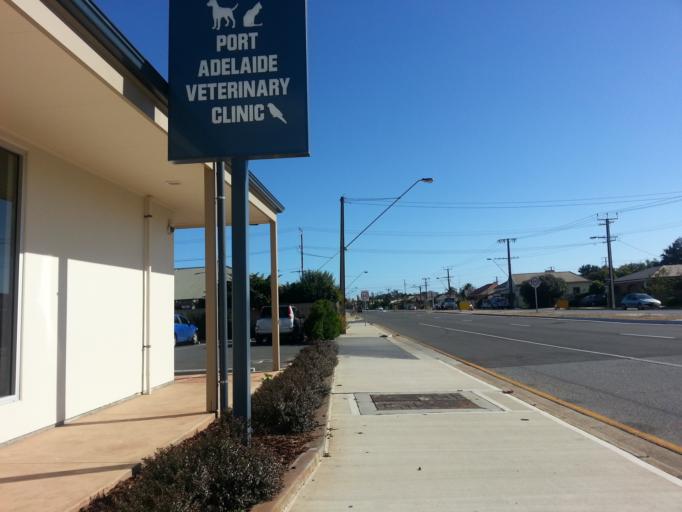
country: AU
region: South Australia
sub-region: Port Adelaide Enfield
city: Birkenhead
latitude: -34.8462
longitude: 138.4910
